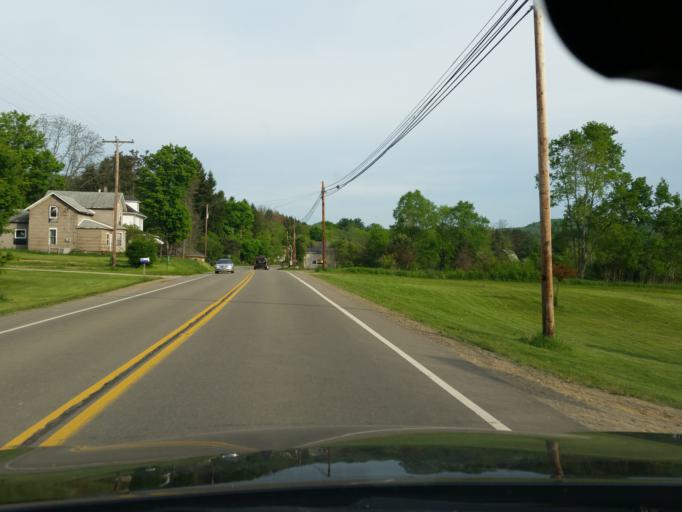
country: US
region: Pennsylvania
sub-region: Warren County
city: Sheffield
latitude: 41.6777
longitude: -79.0275
